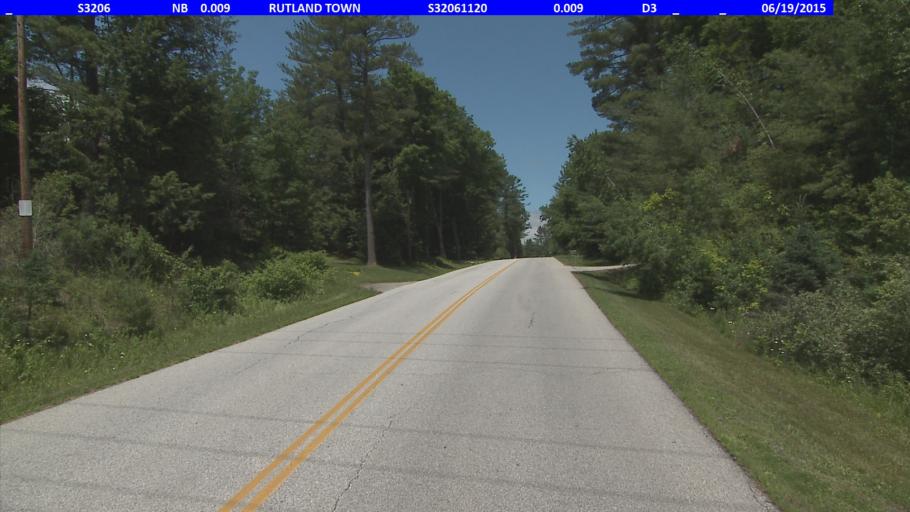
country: US
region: Vermont
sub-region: Rutland County
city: Rutland
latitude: 43.6300
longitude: -72.9885
